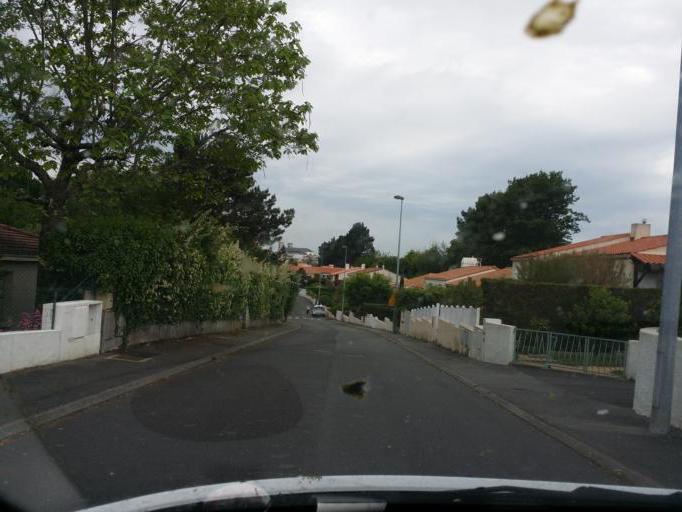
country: FR
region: Pays de la Loire
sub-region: Departement de la Vendee
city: La Roche-sur-Yon
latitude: 46.6668
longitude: -1.4125
